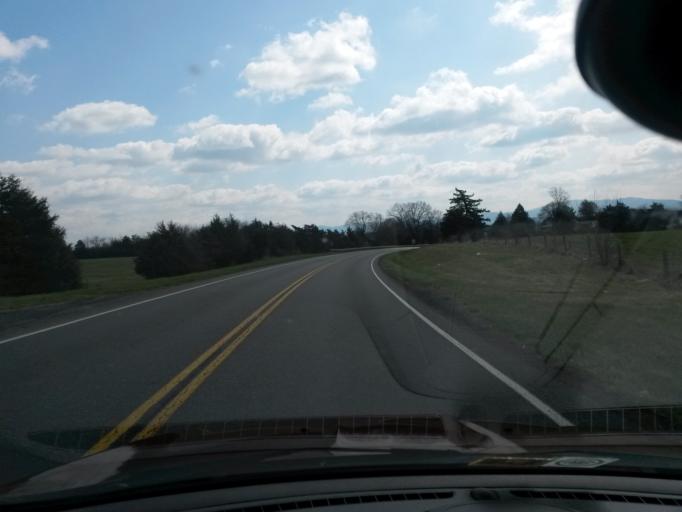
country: US
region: Virginia
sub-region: Augusta County
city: Weyers Cave
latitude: 38.2888
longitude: -78.9223
